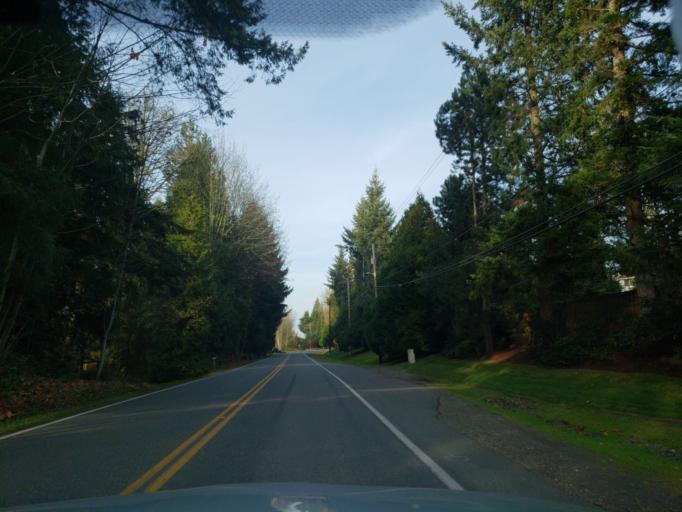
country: US
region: Washington
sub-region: Snohomish County
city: Maltby
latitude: 47.7913
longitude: -122.1331
